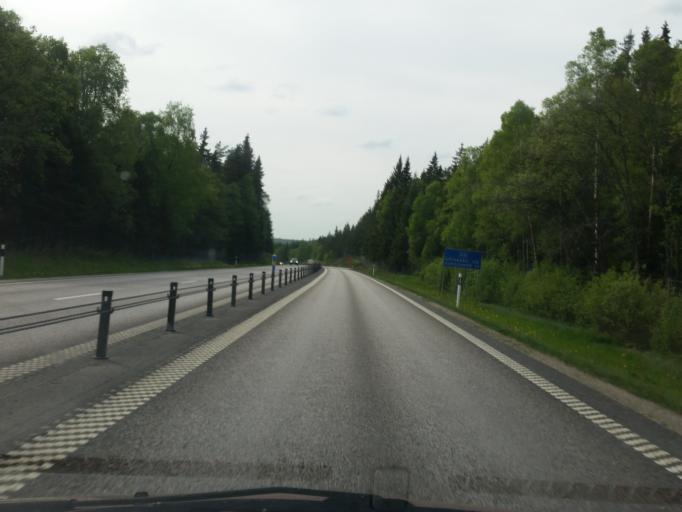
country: SE
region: Vaestra Goetaland
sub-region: Ulricehamns Kommun
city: Ulricehamn
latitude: 57.7928
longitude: 13.6259
